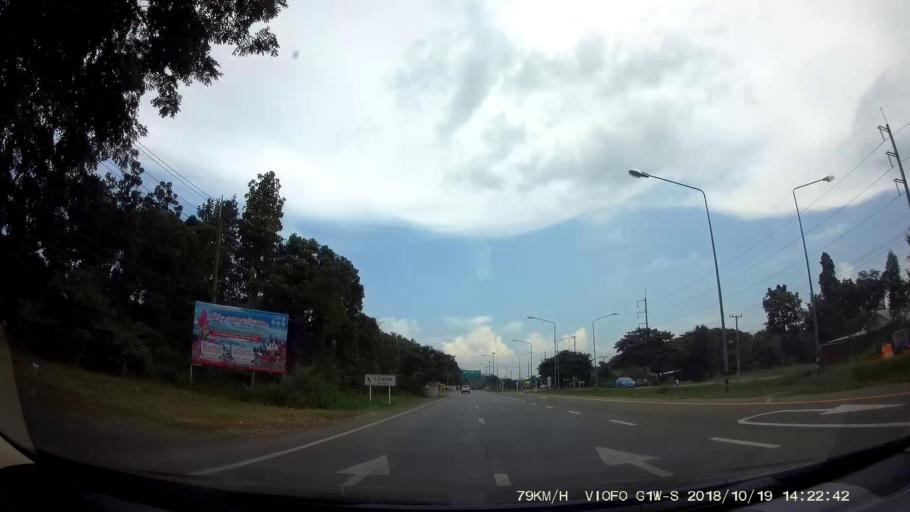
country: TH
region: Chaiyaphum
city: Kaeng Khro
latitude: 16.0654
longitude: 102.2768
